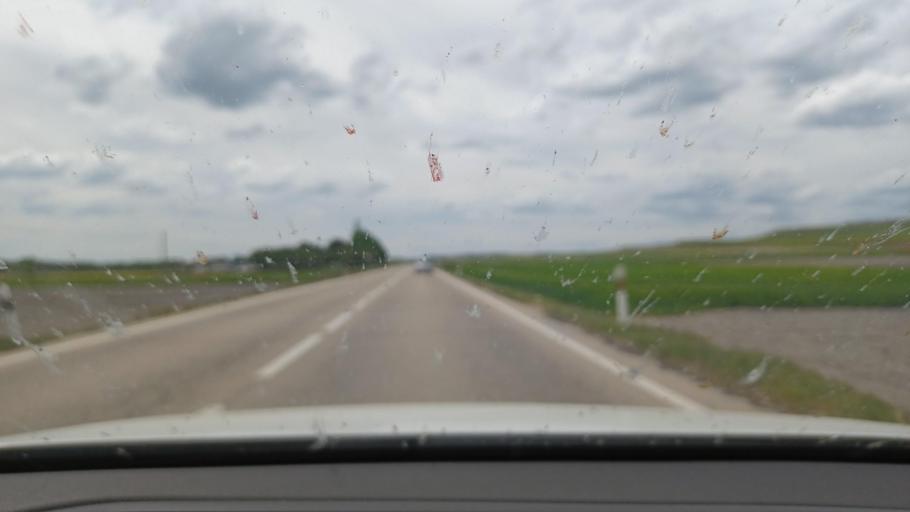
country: ES
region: Castille and Leon
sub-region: Provincia de Segovia
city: Cuellar
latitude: 41.3849
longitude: -4.2562
